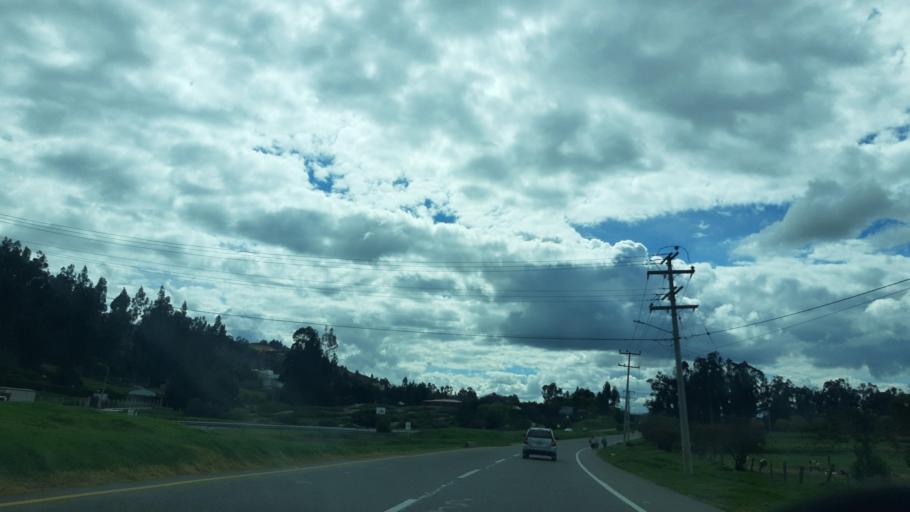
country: CO
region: Cundinamarca
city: Tocancipa
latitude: 4.9709
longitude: -73.8970
